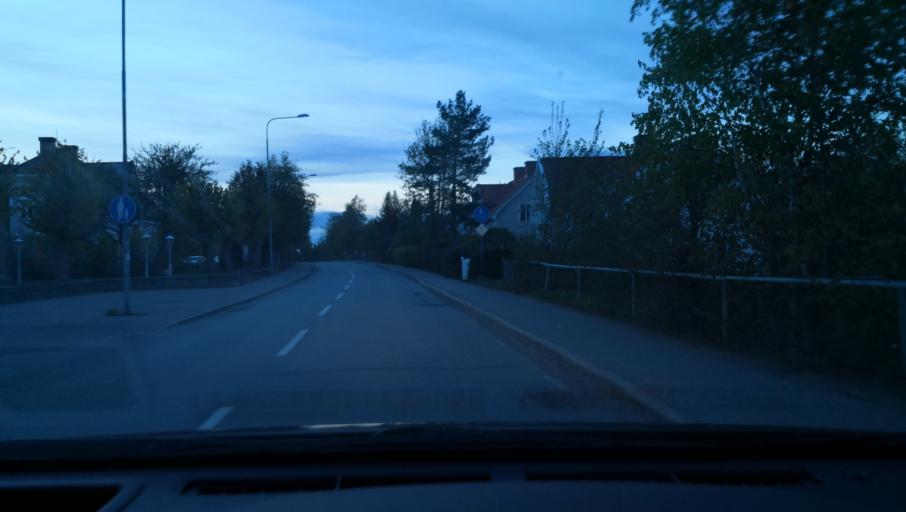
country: SE
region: OErebro
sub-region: Askersunds Kommun
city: Askersund
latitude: 59.0245
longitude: 14.8681
